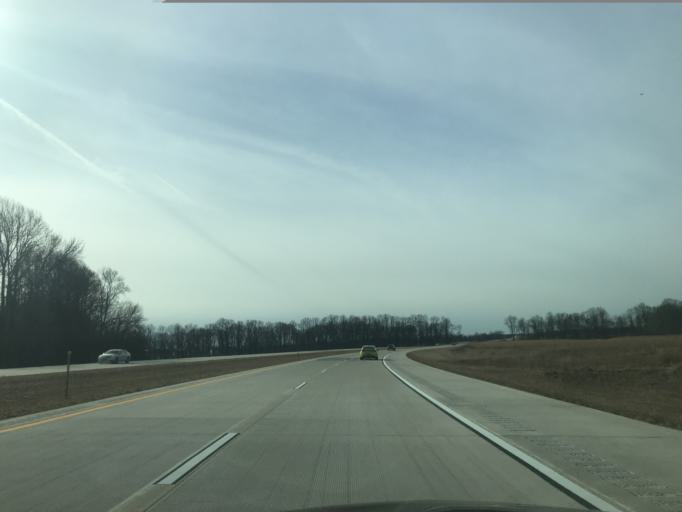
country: US
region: Delaware
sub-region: New Castle County
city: Middletown
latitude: 39.5001
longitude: -75.6962
